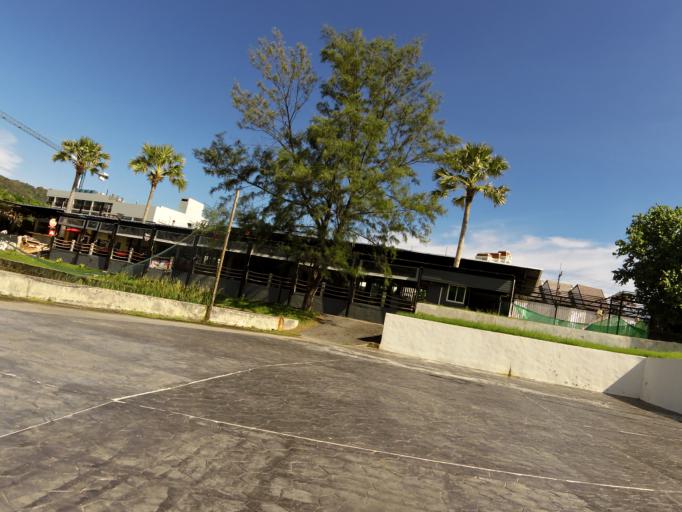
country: TH
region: Phuket
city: Ban Karon
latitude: 7.8512
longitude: 98.2933
